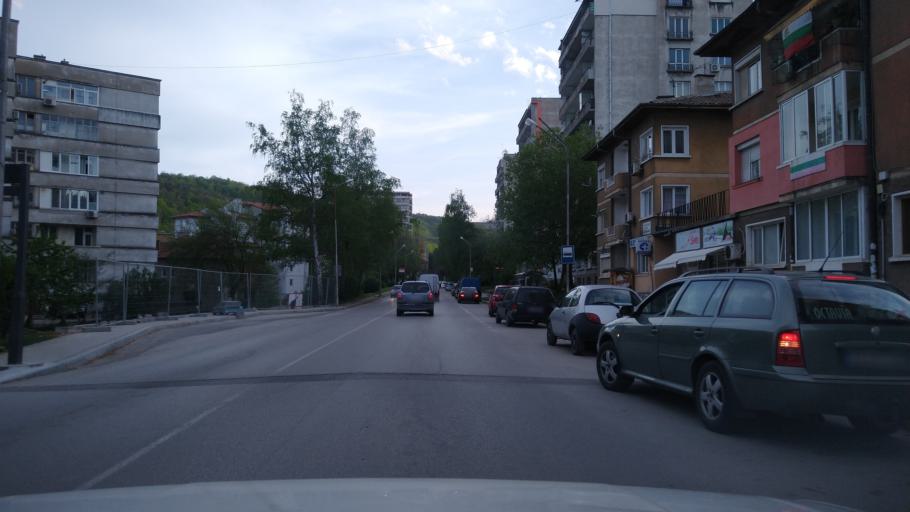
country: BG
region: Gabrovo
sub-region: Obshtina Gabrovo
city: Gabrovo
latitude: 42.8732
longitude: 25.3154
